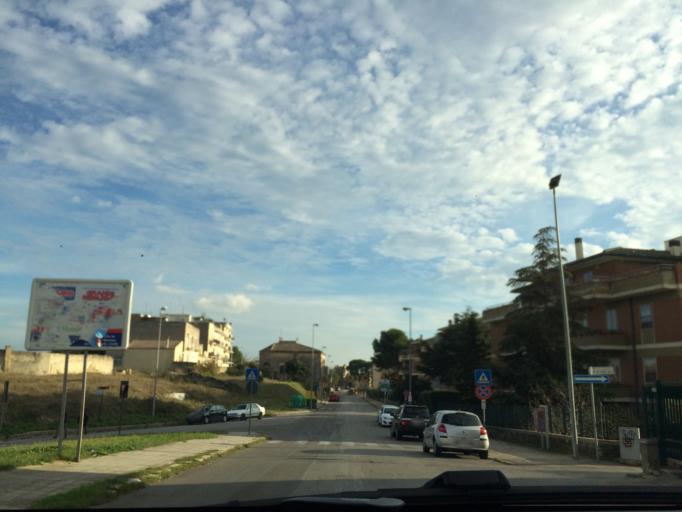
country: IT
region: Basilicate
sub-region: Provincia di Matera
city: Matera
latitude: 40.6557
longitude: 16.6166
